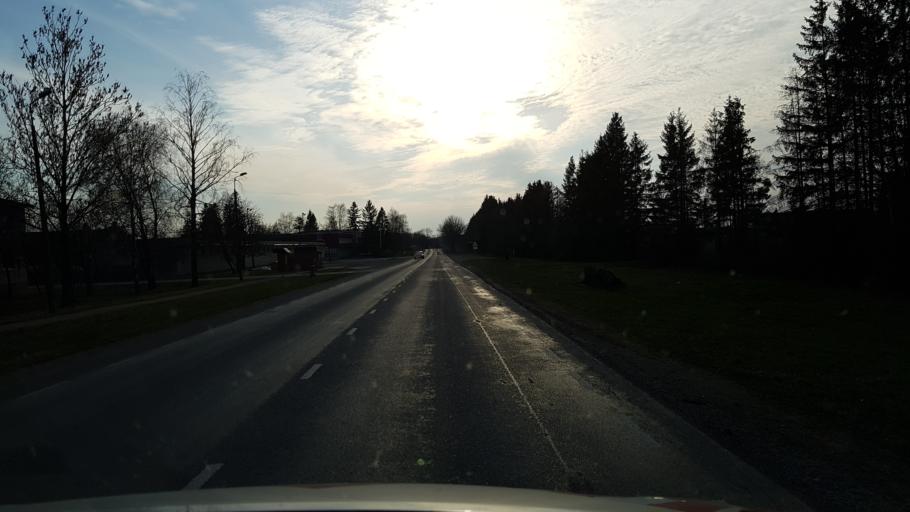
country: EE
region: Laeaene-Virumaa
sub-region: Someru vald
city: Someru
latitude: 59.3648
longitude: 26.4085
